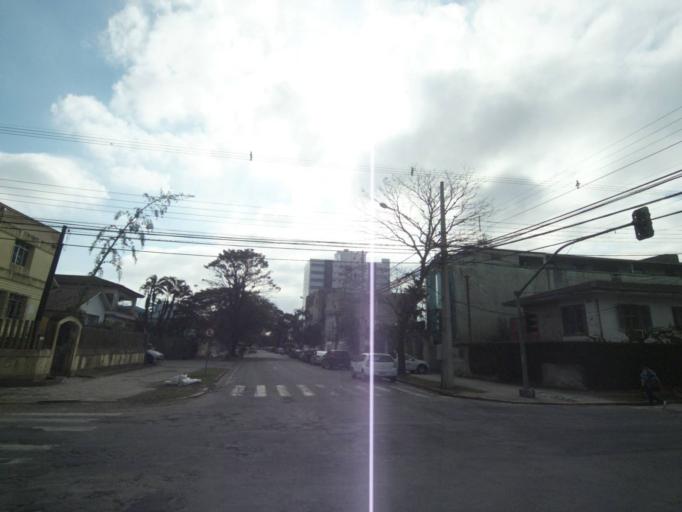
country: BR
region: Parana
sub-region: Paranagua
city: Paranagua
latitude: -25.5169
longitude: -48.5112
